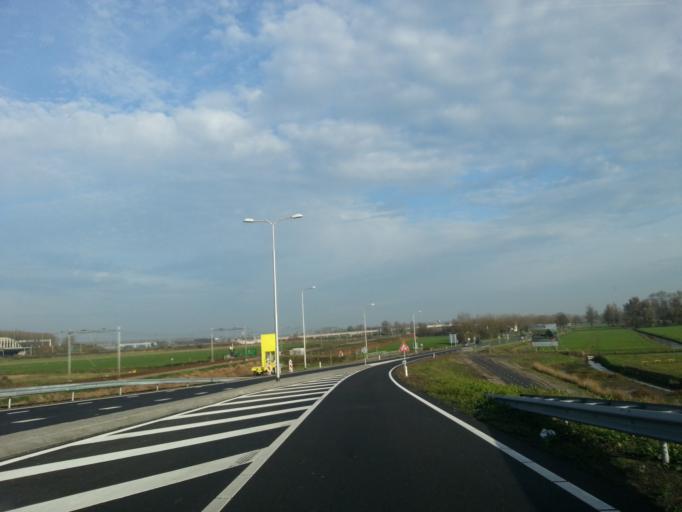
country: NL
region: South Holland
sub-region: Gemeente Waddinxveen
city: Waddinxveen
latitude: 52.0031
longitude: 4.6573
